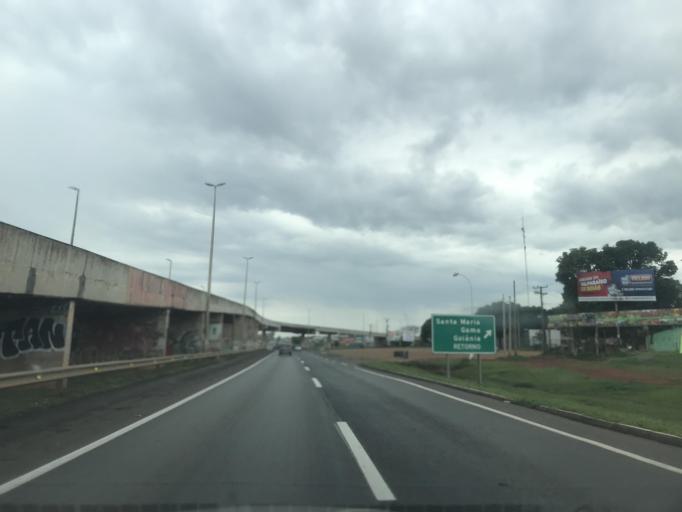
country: BR
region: Federal District
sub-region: Brasilia
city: Brasilia
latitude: -15.9985
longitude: -47.9851
